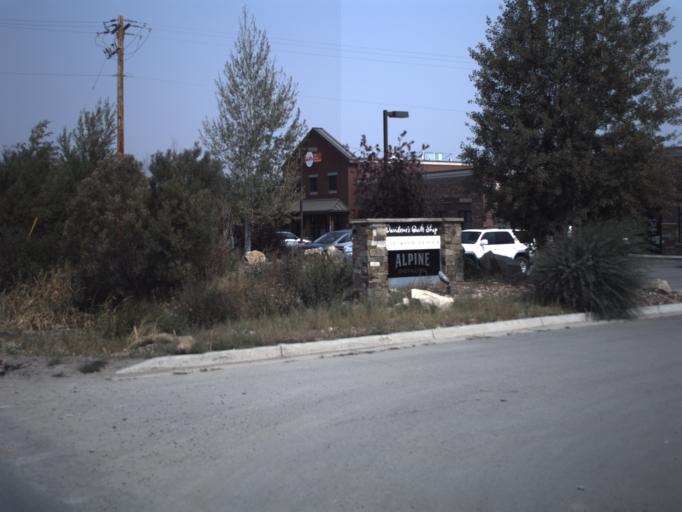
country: US
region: Utah
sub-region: Summit County
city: Snyderville
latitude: 40.7346
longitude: -111.4996
